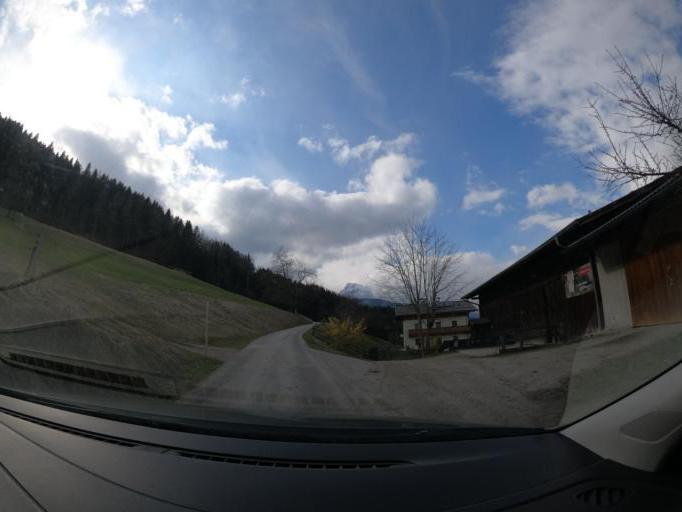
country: AT
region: Salzburg
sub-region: Politischer Bezirk Sankt Johann im Pongau
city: Pfarrwerfen
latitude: 47.4489
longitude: 13.1999
